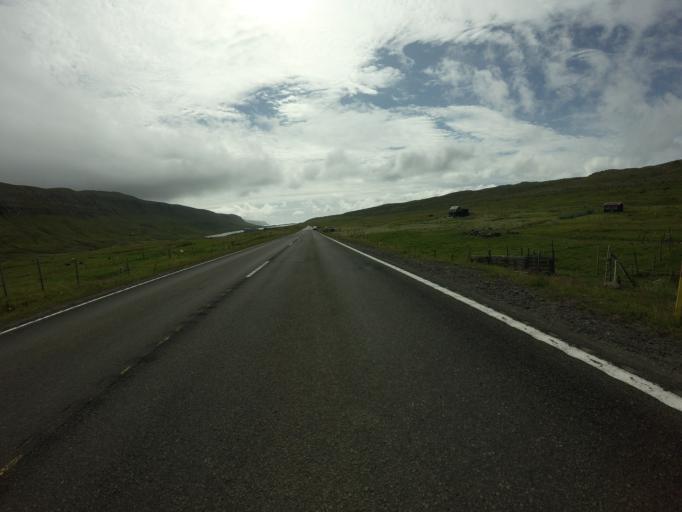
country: FO
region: Sandoy
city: Sandur
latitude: 61.8629
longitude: -6.8371
